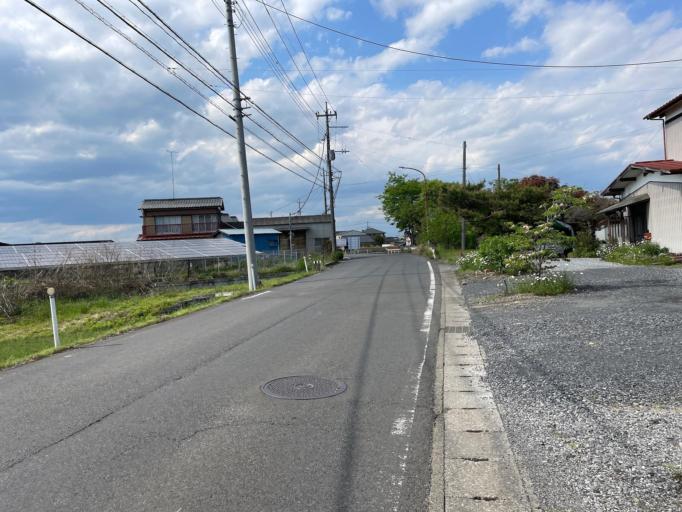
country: JP
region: Tochigi
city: Tochigi
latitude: 36.4086
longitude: 139.7355
